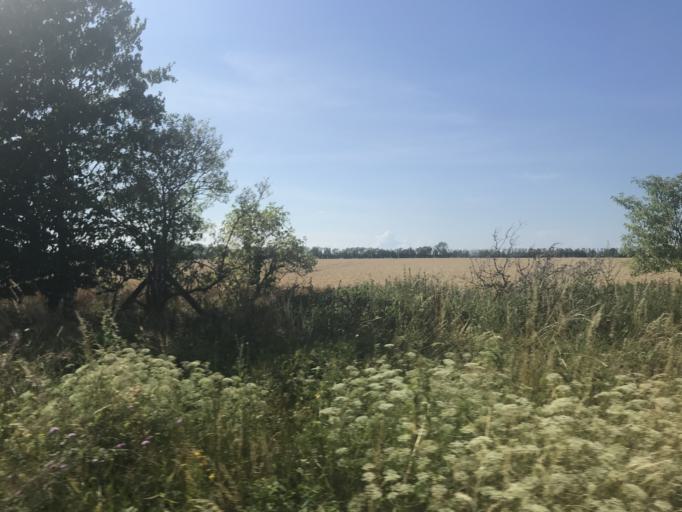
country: PL
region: West Pomeranian Voivodeship
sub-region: Powiat policki
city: Przeclaw
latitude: 53.3898
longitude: 14.4732
